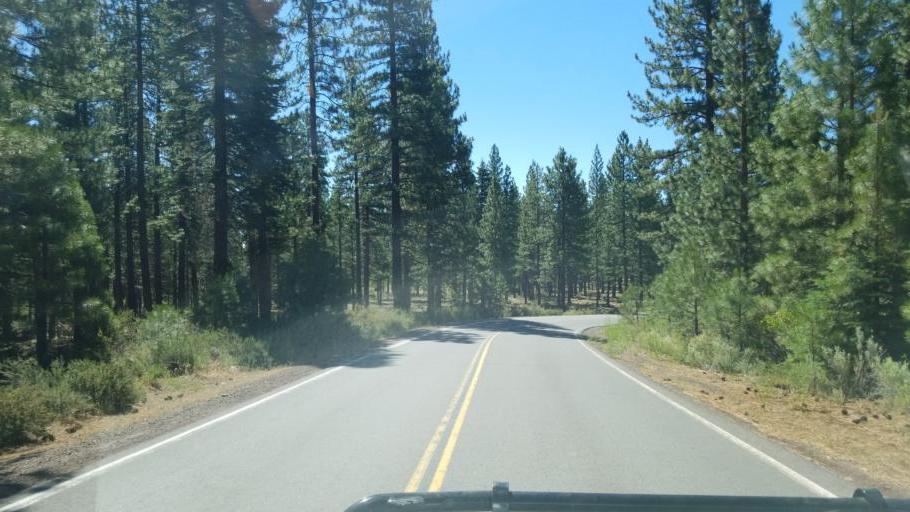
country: US
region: California
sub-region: Lassen County
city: Susanville
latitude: 40.4287
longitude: -120.7279
